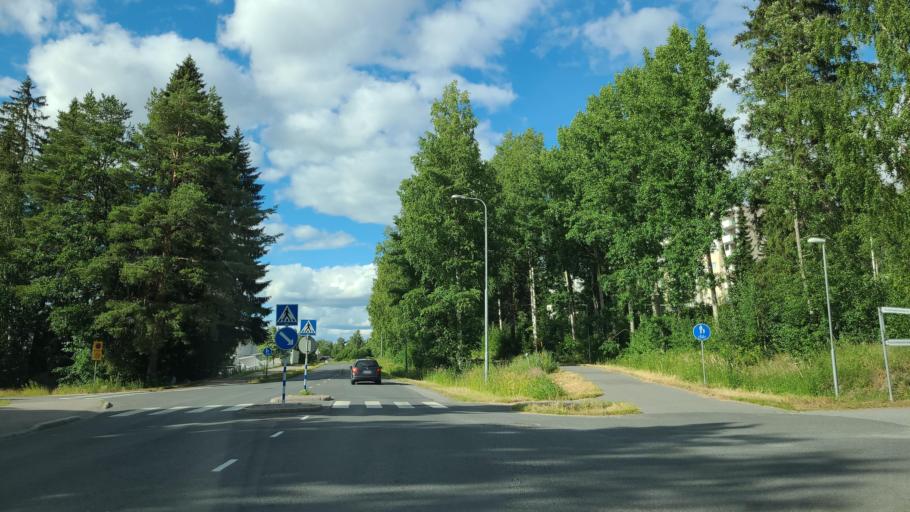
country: FI
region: Northern Savo
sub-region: Kuopio
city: Kuopio
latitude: 62.9329
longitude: 27.6332
